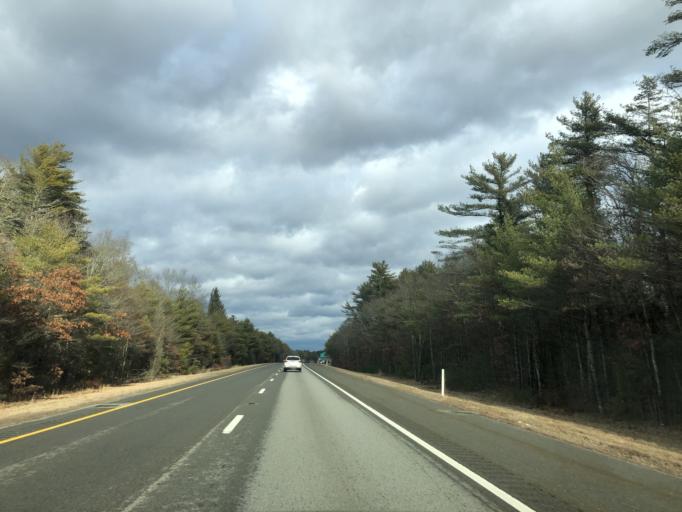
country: US
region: Massachusetts
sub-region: Plymouth County
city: Marion Center
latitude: 41.7188
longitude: -70.7820
